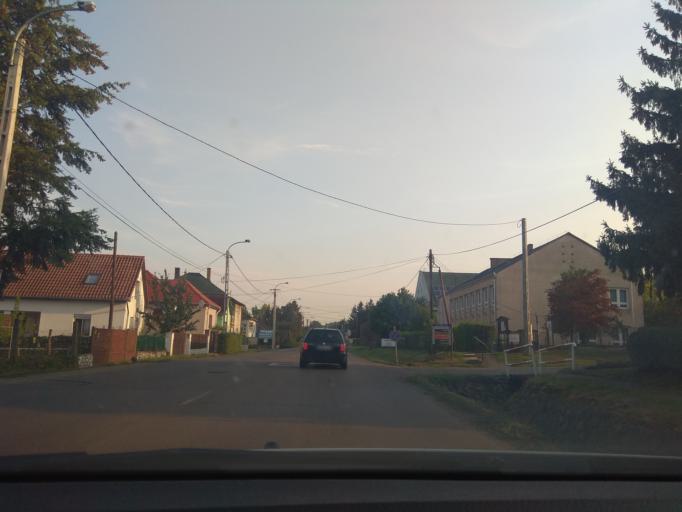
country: HU
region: Heves
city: Andornaktalya
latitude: 47.8575
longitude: 20.4069
